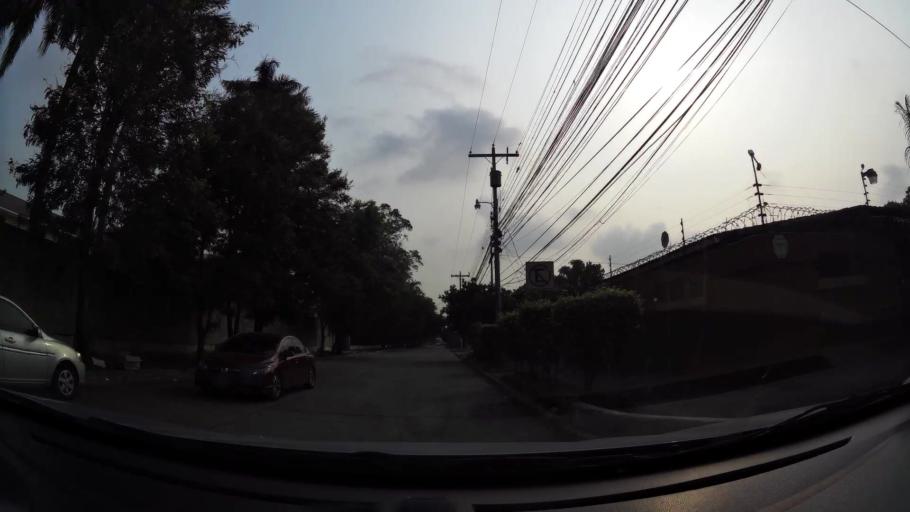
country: HN
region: Cortes
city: Armenta
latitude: 15.4964
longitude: -88.0387
